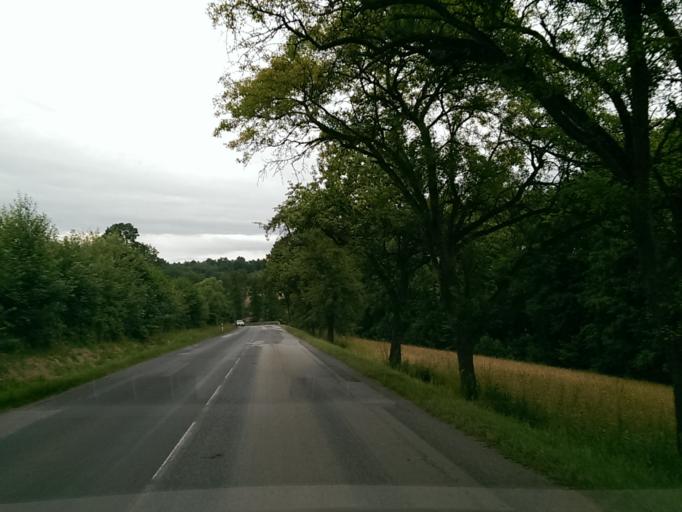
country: CZ
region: Liberecky
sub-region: Okres Semily
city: Turnov
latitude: 50.5891
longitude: 15.1893
